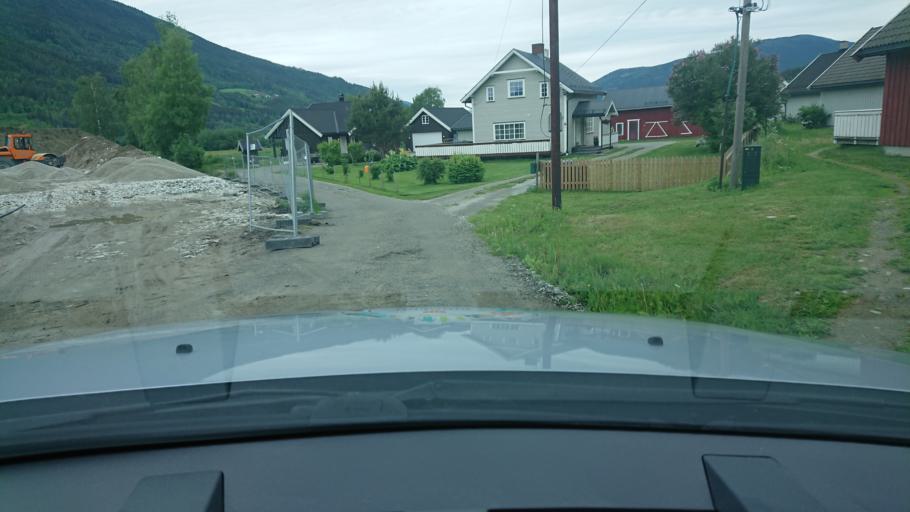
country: NO
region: Oppland
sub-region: Ringebu
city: Ringebu
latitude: 61.5287
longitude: 10.1289
